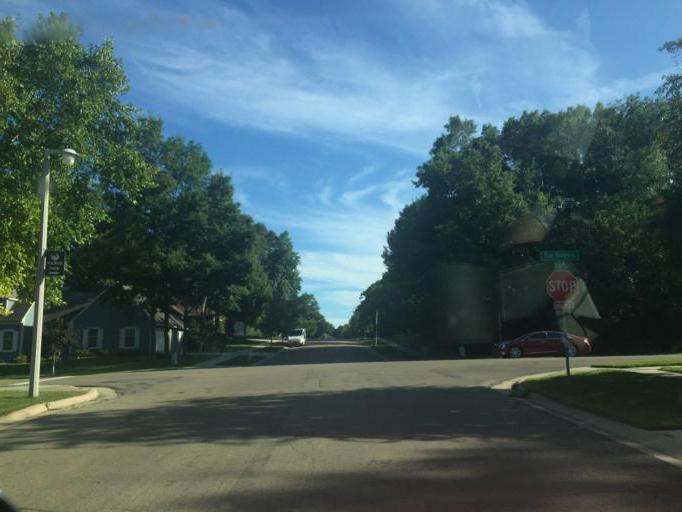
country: US
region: Minnesota
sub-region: Olmsted County
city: Rochester
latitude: 44.0111
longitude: -92.4982
